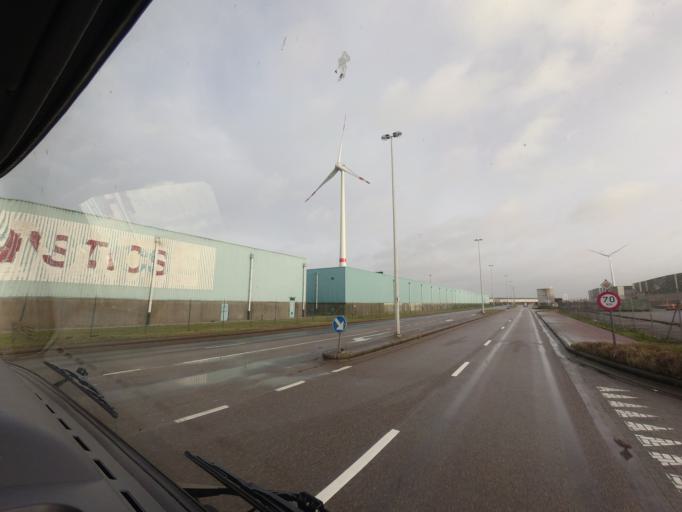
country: BE
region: Flanders
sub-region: Provincie Antwerpen
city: Stabroek
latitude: 51.3146
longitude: 4.3268
